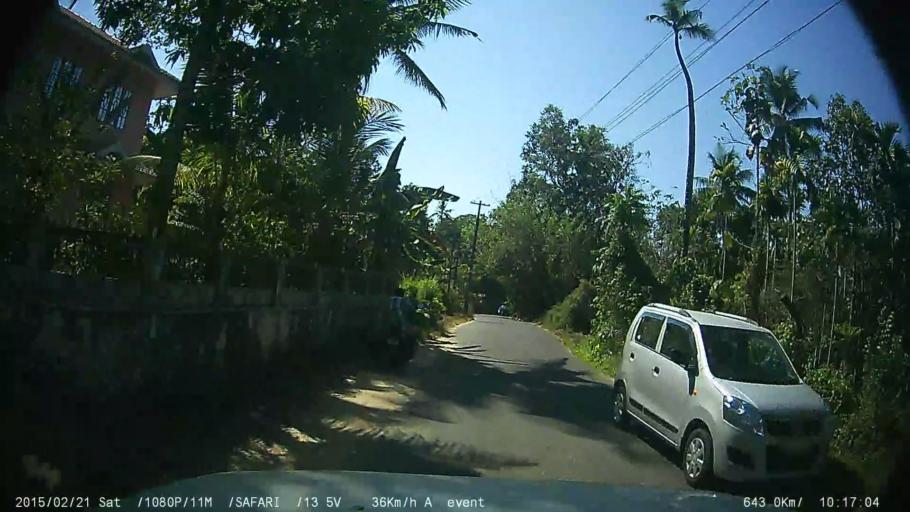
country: IN
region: Kerala
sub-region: Ernakulam
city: Muvattupuzha
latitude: 9.8796
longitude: 76.6467
